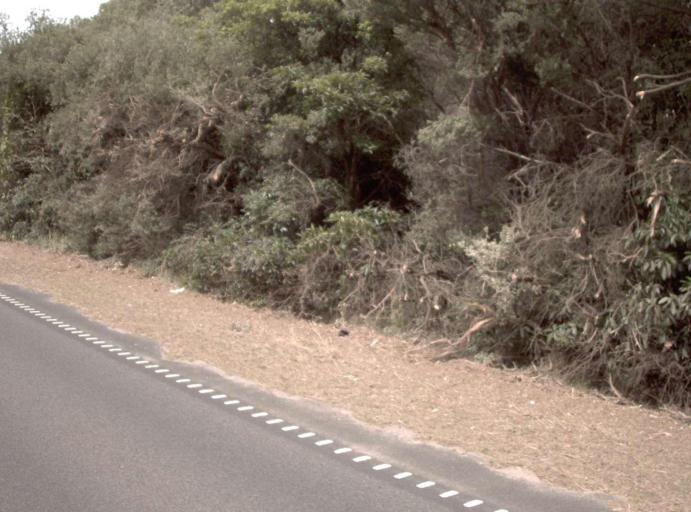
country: AU
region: Victoria
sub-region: Mornington Peninsula
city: Mornington
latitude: -38.2625
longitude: 145.0743
